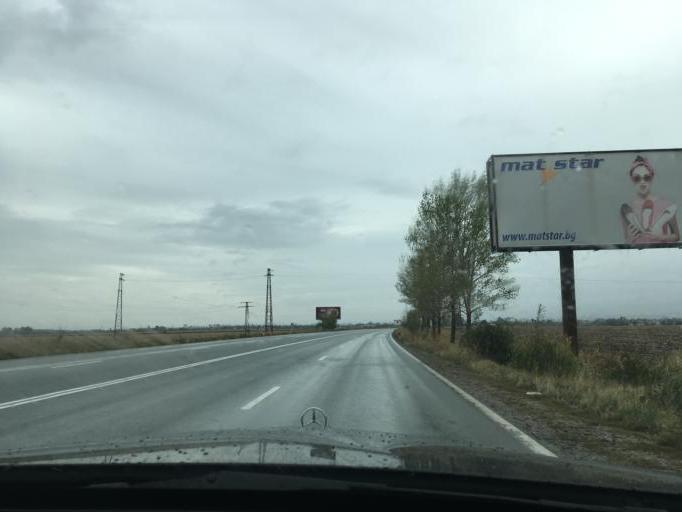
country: BG
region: Sofiya
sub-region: Obshtina Bozhurishte
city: Bozhurishte
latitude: 42.7657
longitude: 23.2131
